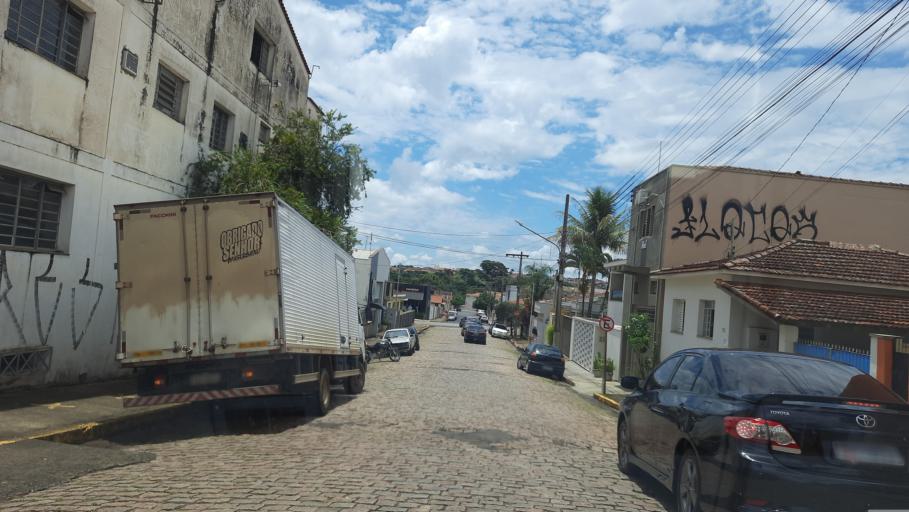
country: BR
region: Sao Paulo
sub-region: Vargem Grande Do Sul
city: Vargem Grande do Sul
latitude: -21.8340
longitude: -46.8951
